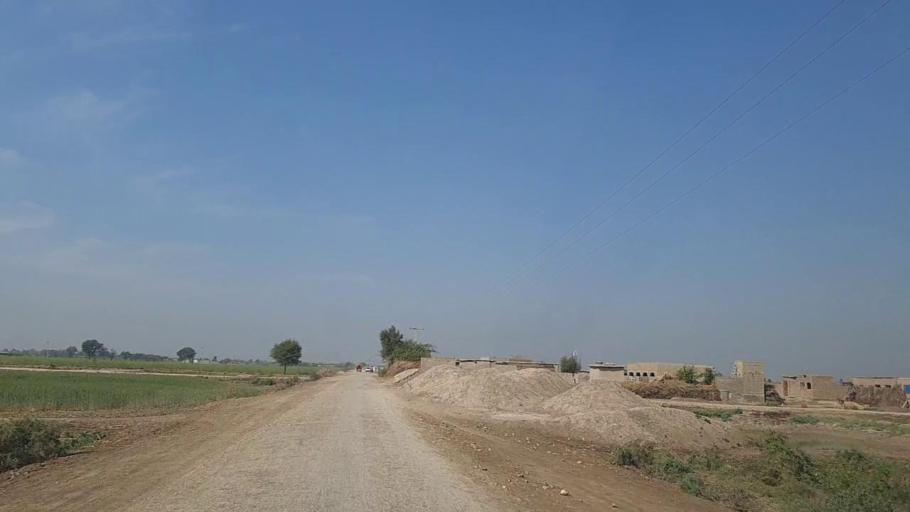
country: PK
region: Sindh
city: Mirpur Khas
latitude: 25.4824
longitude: 68.9972
